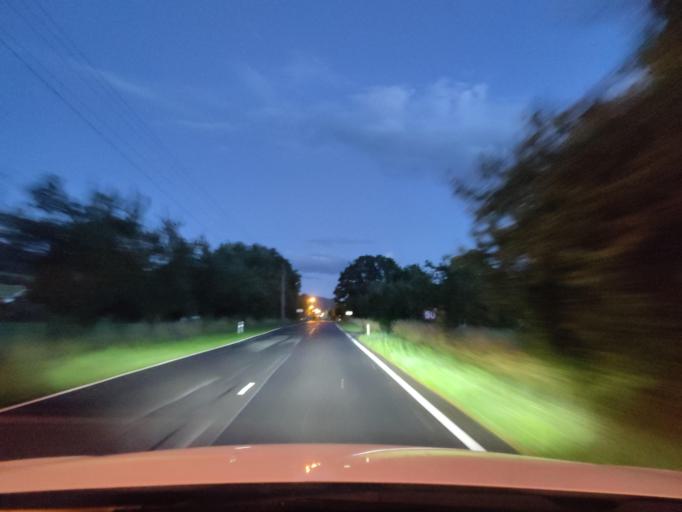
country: CZ
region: Olomoucky
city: Zlate Hory
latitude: 50.2711
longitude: 17.3934
